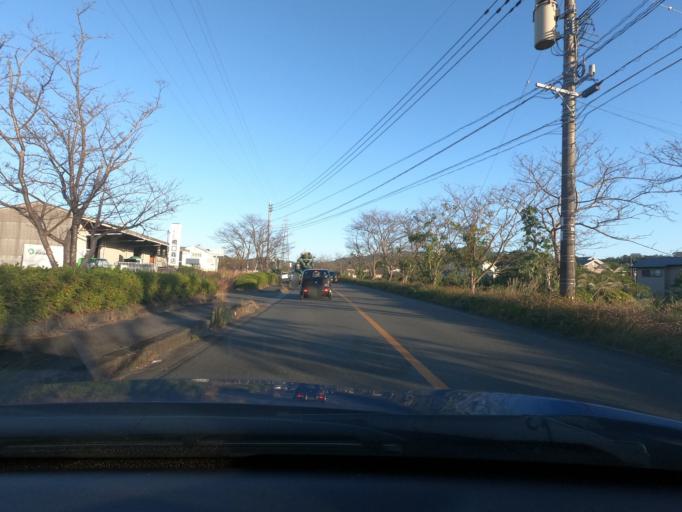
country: JP
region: Kagoshima
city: Satsumasendai
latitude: 31.8085
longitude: 130.3227
